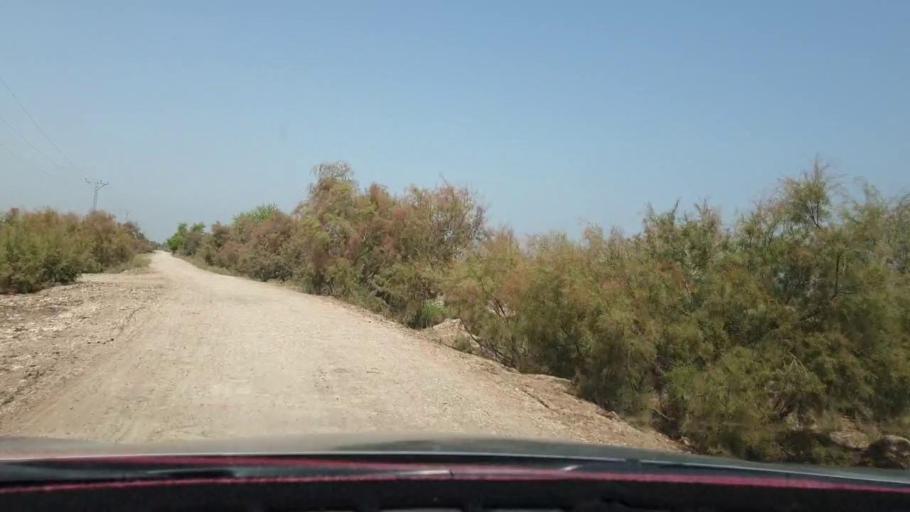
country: PK
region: Sindh
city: Warah
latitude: 27.4099
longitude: 67.6984
